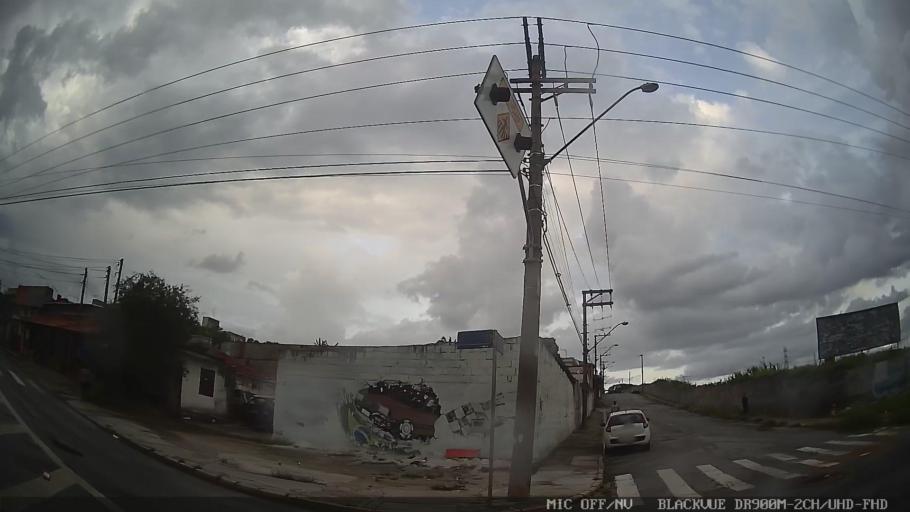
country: BR
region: Sao Paulo
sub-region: Mogi das Cruzes
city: Mogi das Cruzes
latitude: -23.5449
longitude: -46.1840
